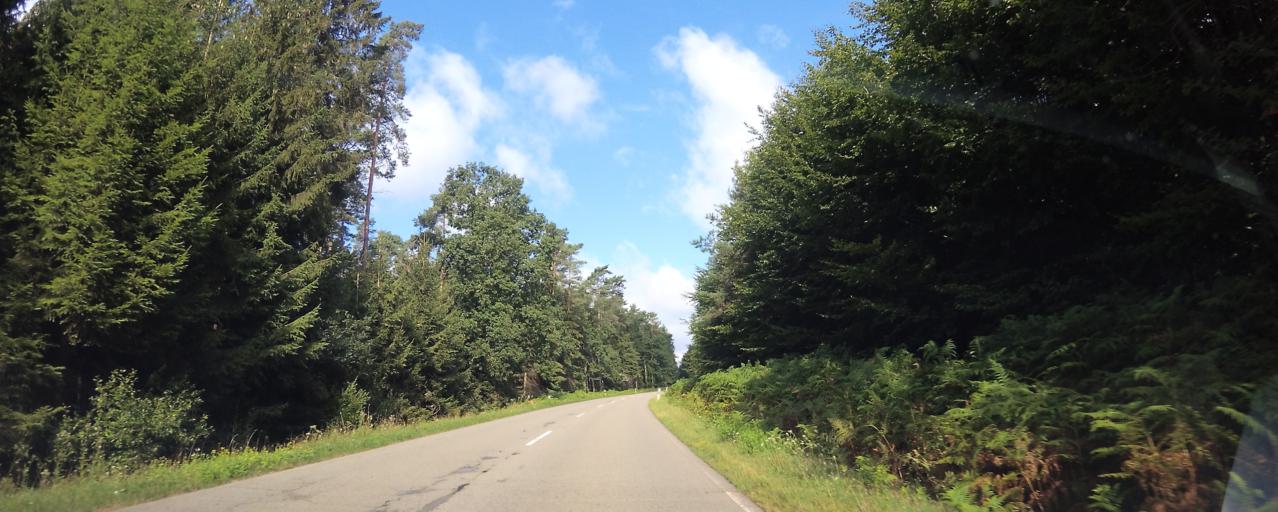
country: DE
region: Rheinland-Pfalz
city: Dierscheid
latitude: 49.8817
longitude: 6.7253
